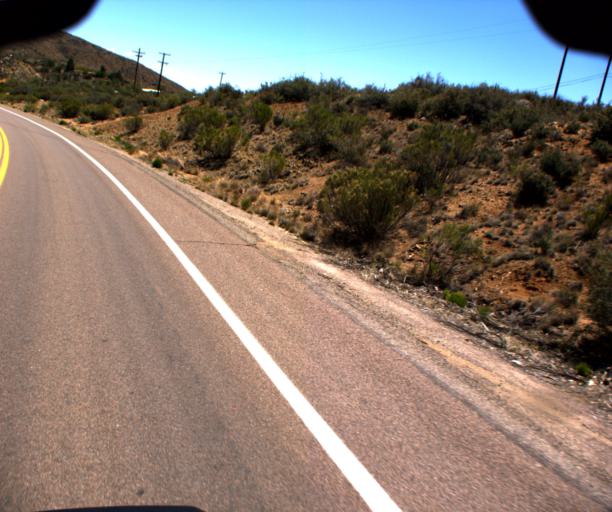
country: US
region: Arizona
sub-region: Yavapai County
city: Bagdad
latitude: 34.5653
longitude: -113.1733
